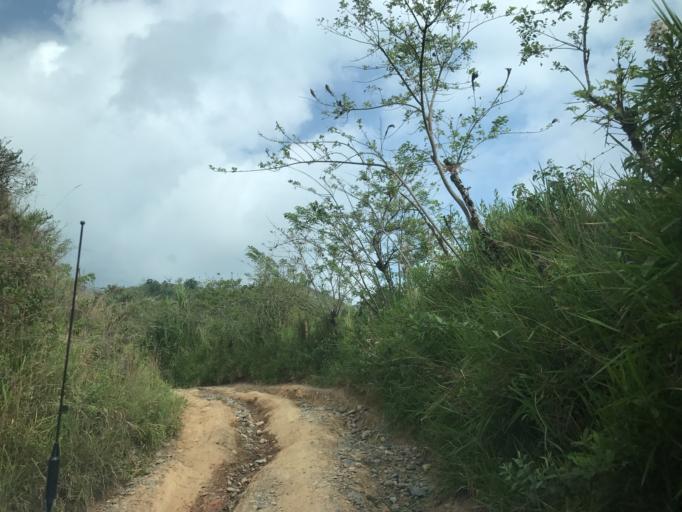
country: CO
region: Valle del Cauca
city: Obando
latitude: 4.5660
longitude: -75.8790
